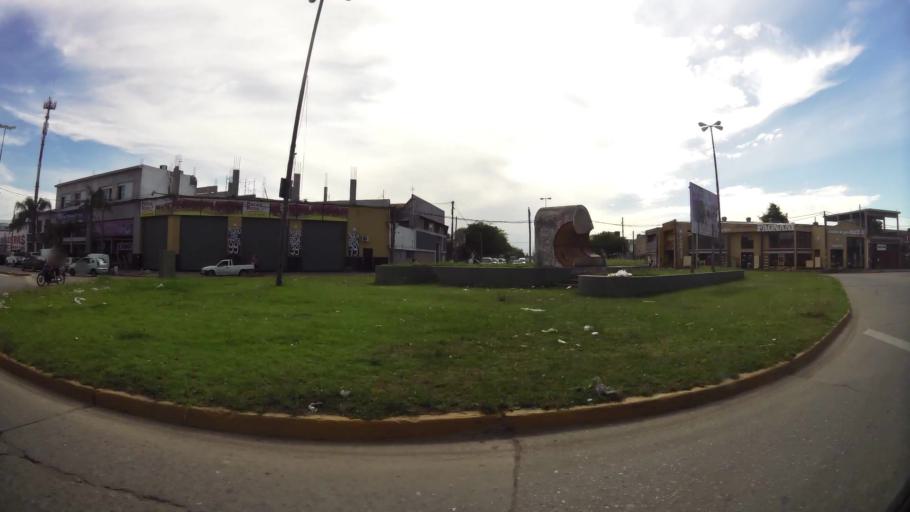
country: AR
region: Santa Fe
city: Granadero Baigorria
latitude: -32.9203
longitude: -60.7134
